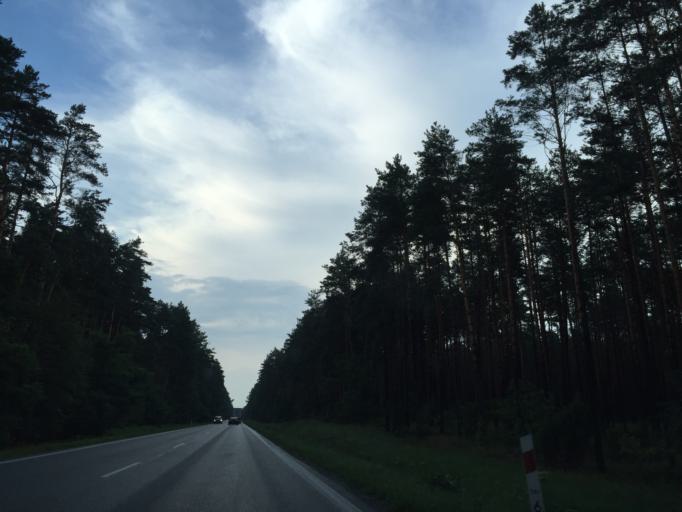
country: PL
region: Masovian Voivodeship
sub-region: Powiat ostrowski
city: Brok
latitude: 52.7091
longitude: 21.8478
